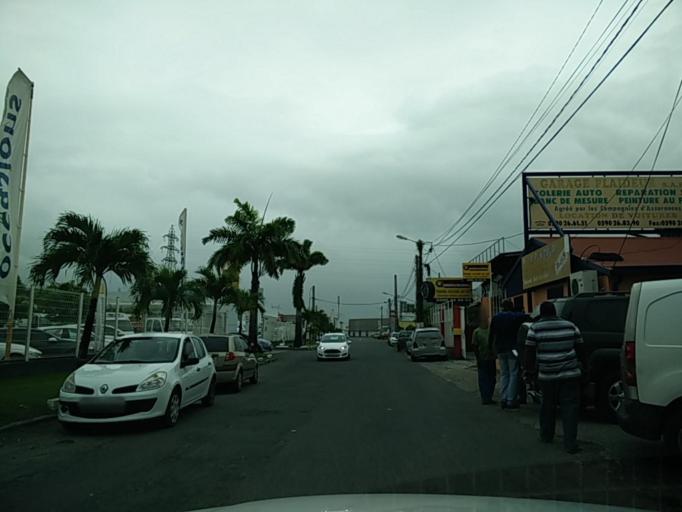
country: GP
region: Guadeloupe
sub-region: Guadeloupe
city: Pointe-a-Pitre
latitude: 16.2531
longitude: -61.5559
